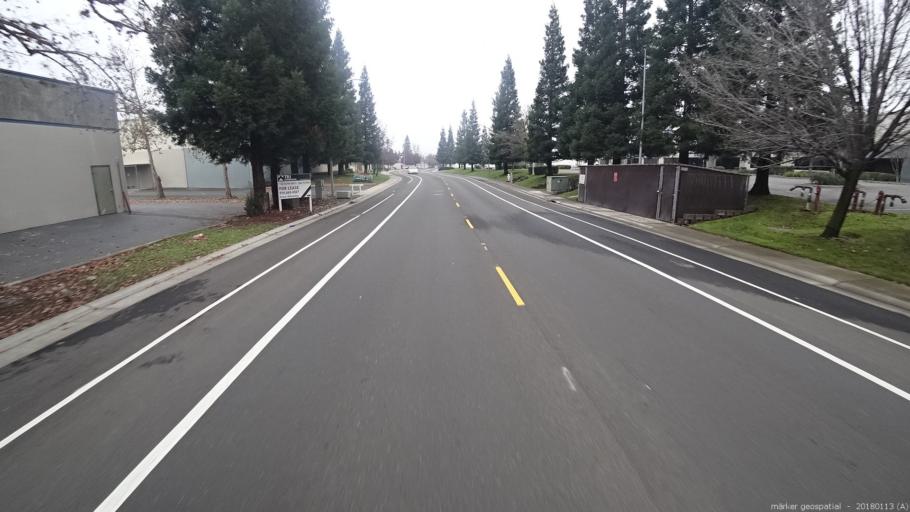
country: US
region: California
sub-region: Sacramento County
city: Gold River
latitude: 38.6006
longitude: -121.2612
